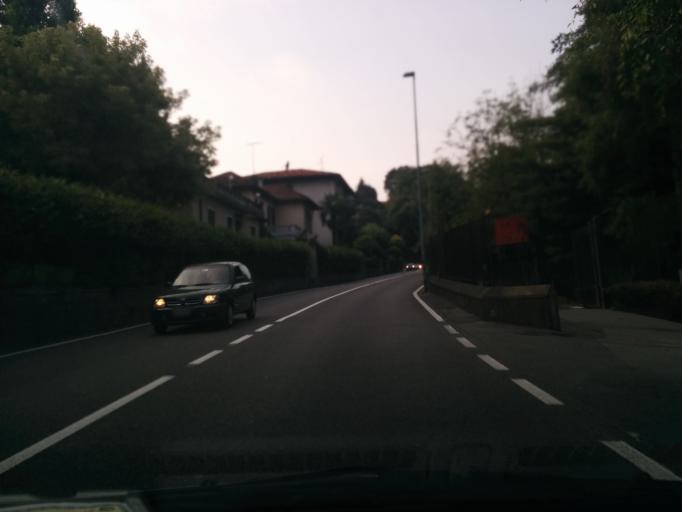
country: IT
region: Lombardy
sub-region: Provincia di Como
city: Brunate
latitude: 45.8029
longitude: 9.1030
